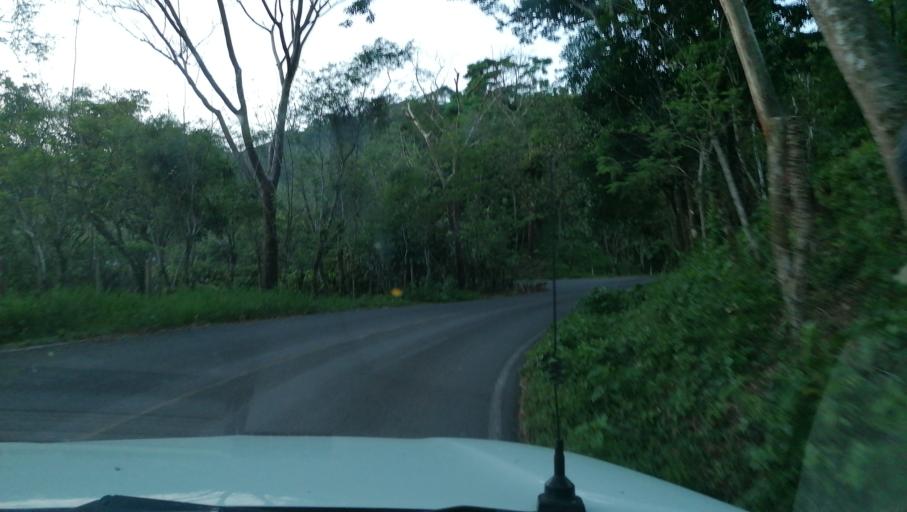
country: MX
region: Chiapas
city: Ostuacan
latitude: 17.4244
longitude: -93.3380
